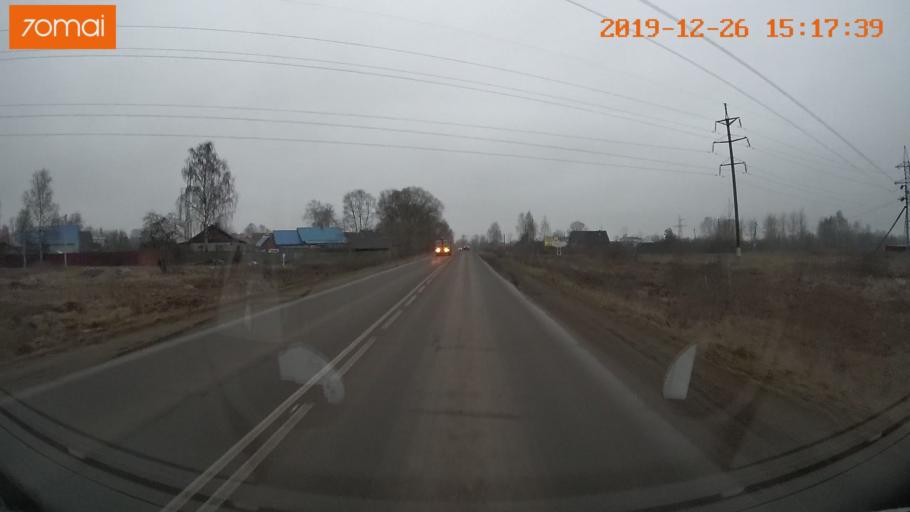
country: RU
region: Jaroslavl
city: Rybinsk
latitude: 58.0750
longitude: 38.8498
